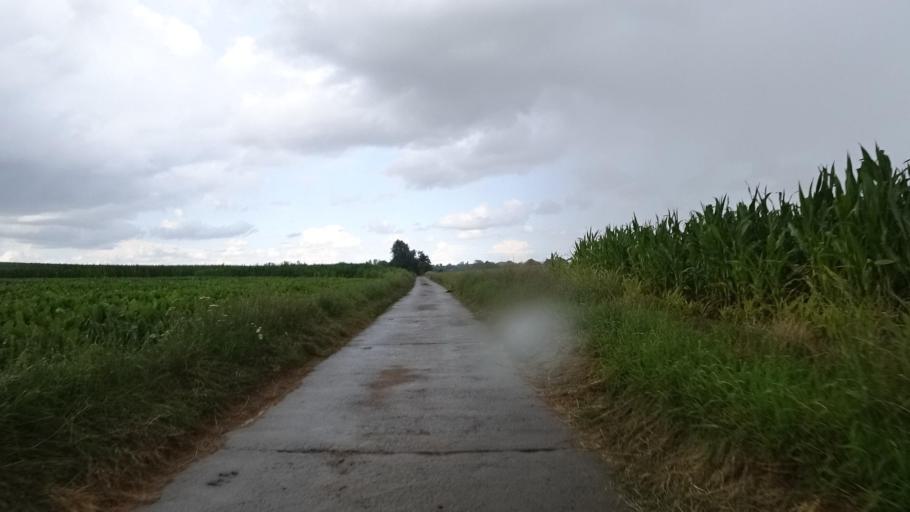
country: BE
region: Wallonia
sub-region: Province du Brabant Wallon
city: Chastre
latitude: 50.5965
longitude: 4.6265
